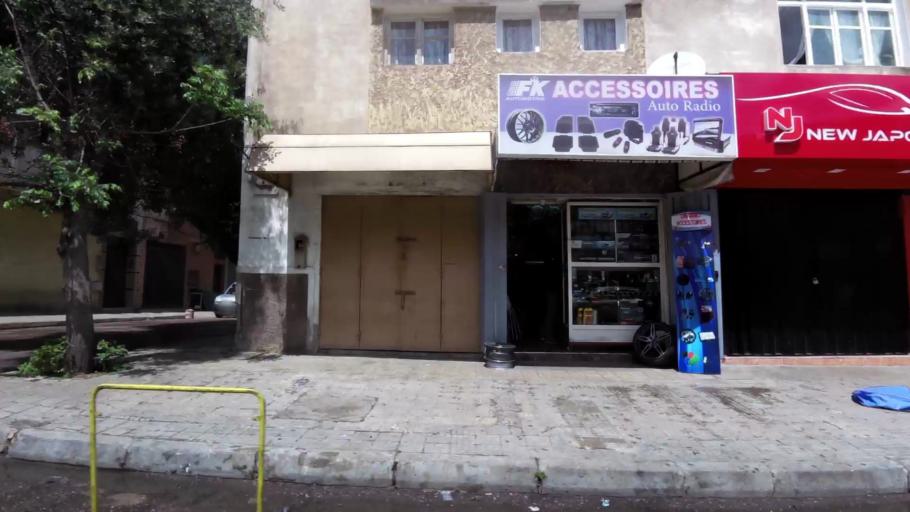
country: MA
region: Grand Casablanca
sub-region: Casablanca
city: Casablanca
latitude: 33.5530
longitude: -7.6777
